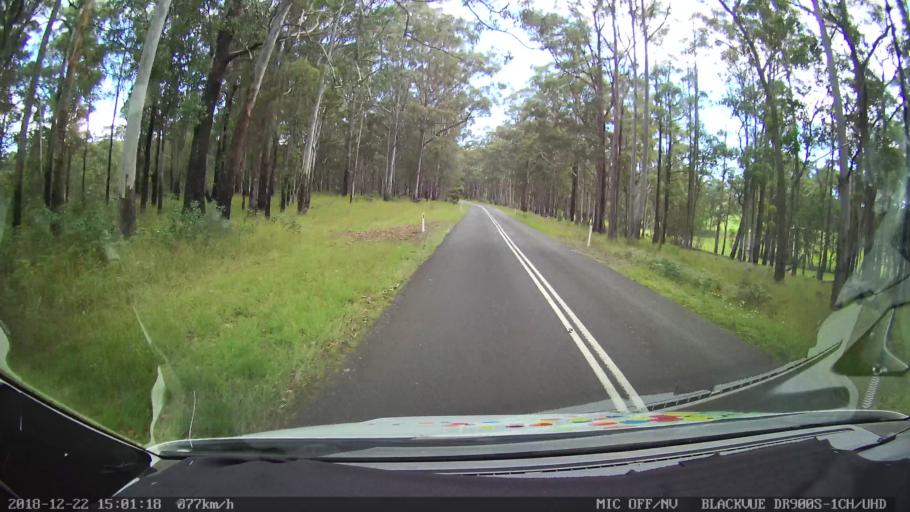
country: AU
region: New South Wales
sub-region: Bellingen
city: Dorrigo
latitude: -30.2530
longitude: 152.4596
